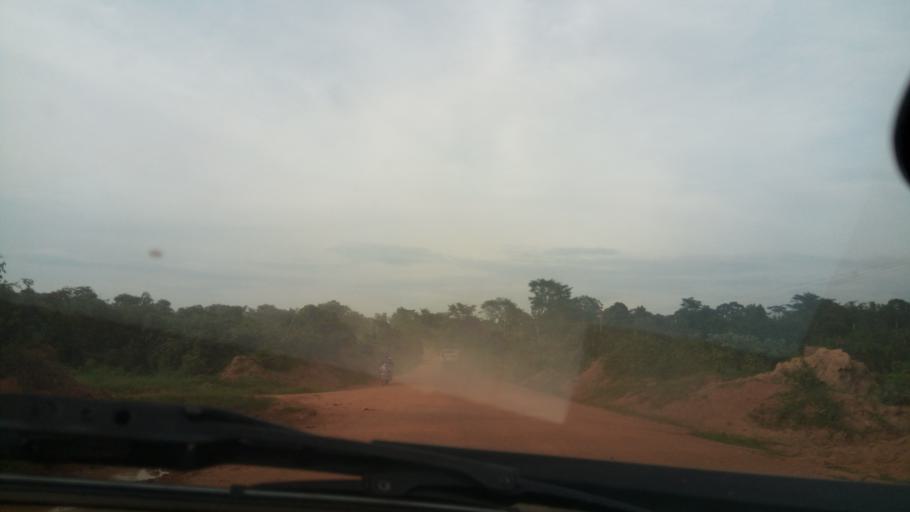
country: UG
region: Central Region
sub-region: Mityana District
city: Mityana
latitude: 0.5552
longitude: 32.1920
